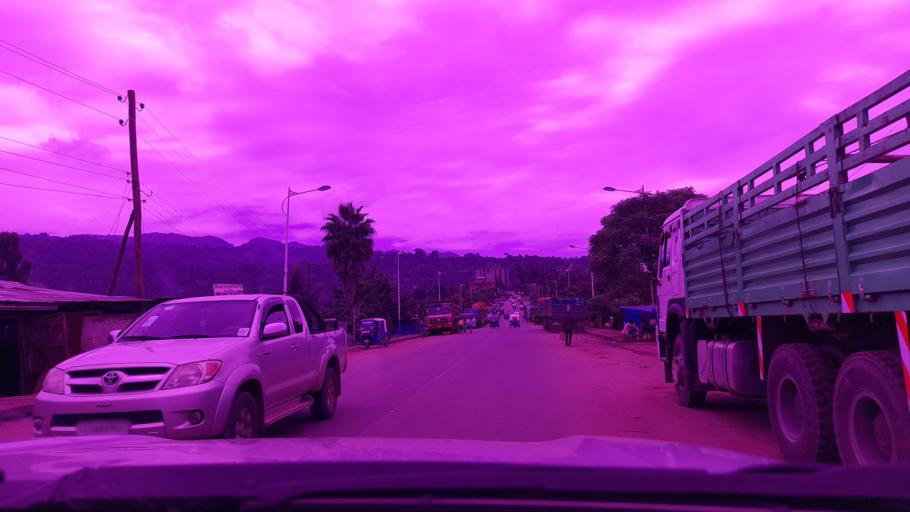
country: ET
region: Southern Nations, Nationalities, and People's Region
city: Mizan Teferi
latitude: 6.9973
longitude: 35.5947
